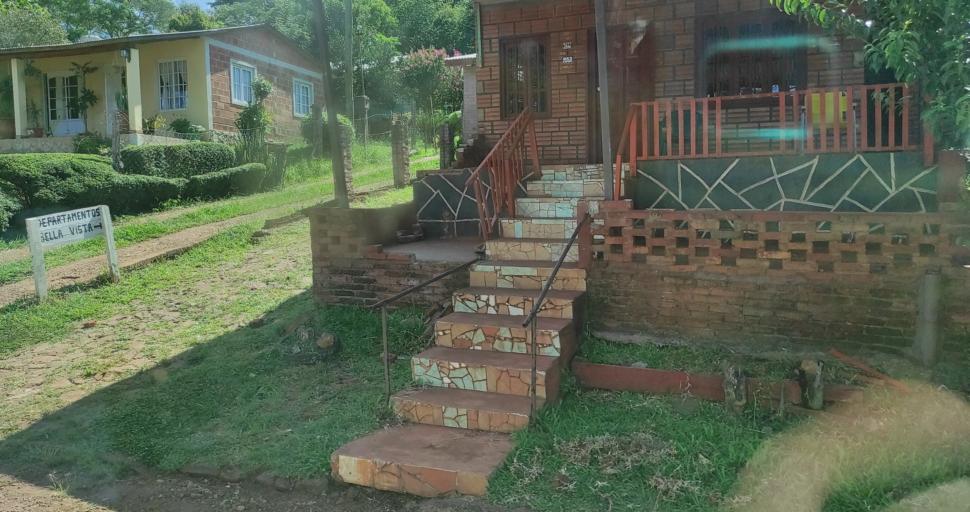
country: AR
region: Misiones
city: El Soberbio
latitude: -27.2913
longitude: -54.1985
